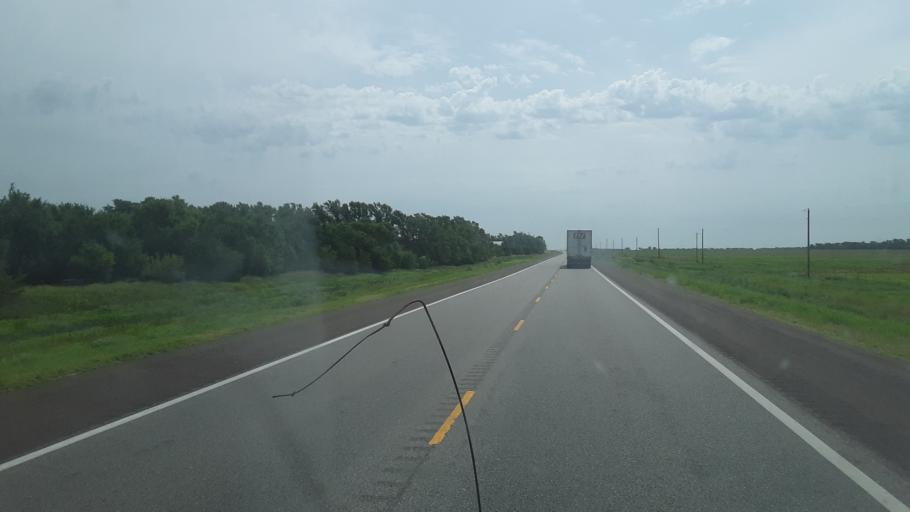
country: US
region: Kansas
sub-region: Reno County
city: Nickerson
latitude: 37.9849
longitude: -98.1413
